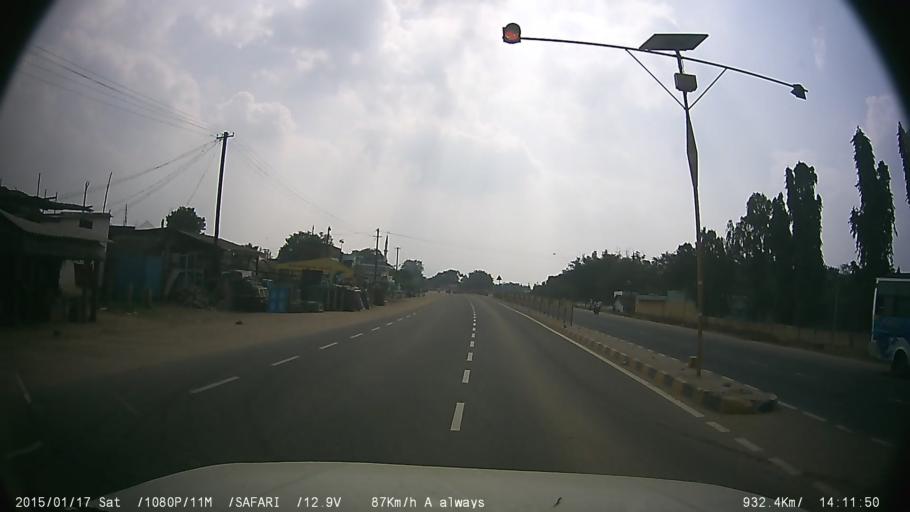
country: IN
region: Tamil Nadu
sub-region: Vellore
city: Ambur
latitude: 12.7916
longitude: 78.7277
